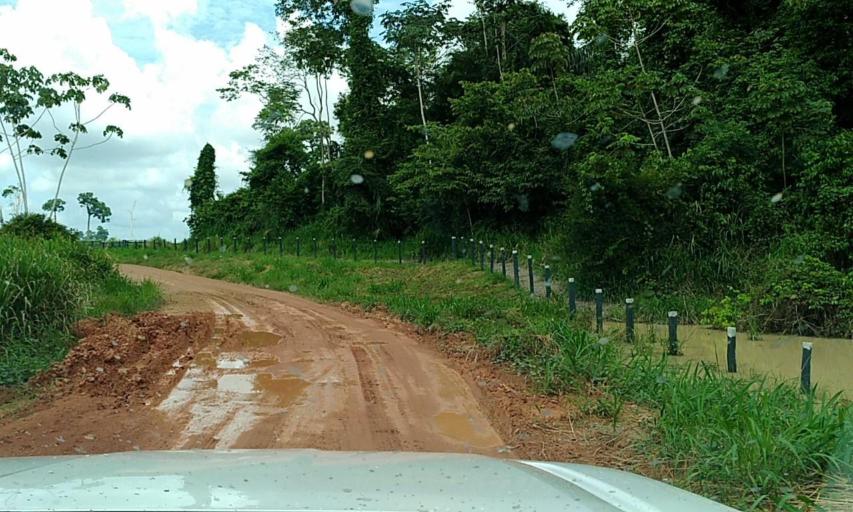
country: BR
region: Para
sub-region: Senador Jose Porfirio
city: Senador Jose Porfirio
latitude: -2.5213
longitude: -51.8505
